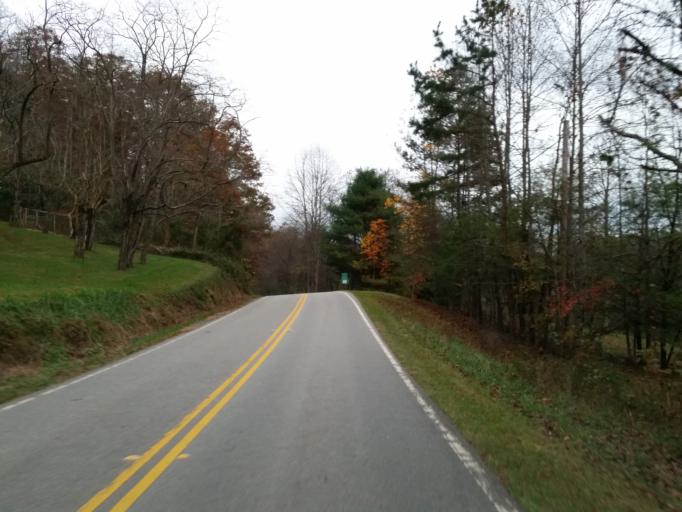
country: US
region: Georgia
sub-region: Union County
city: Blairsville
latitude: 34.7213
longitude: -84.0771
